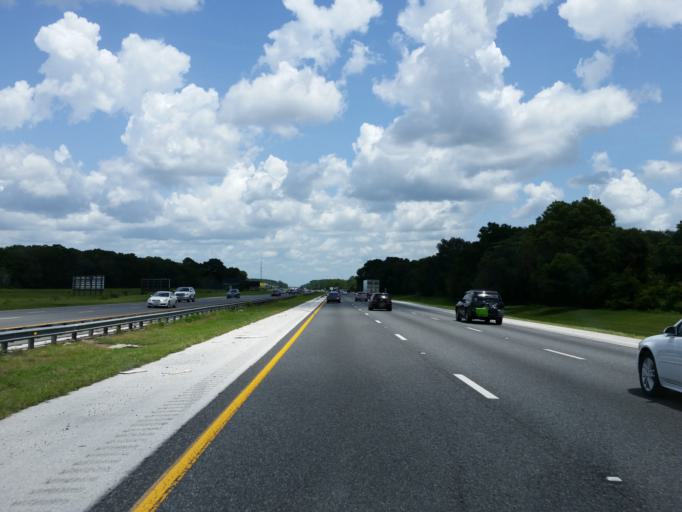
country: US
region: Florida
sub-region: Marion County
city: Belleview
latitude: 28.9625
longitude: -82.1249
